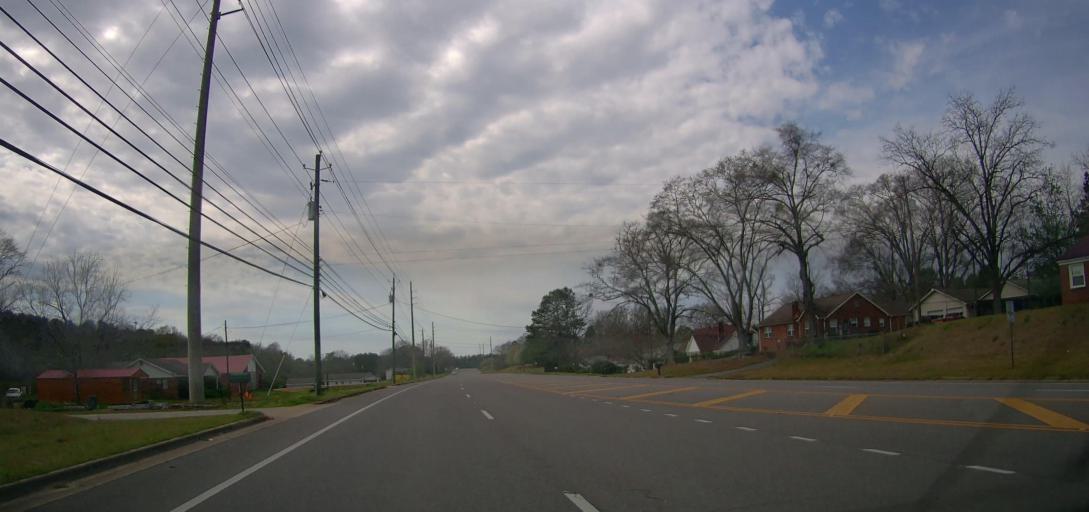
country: US
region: Alabama
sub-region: Marion County
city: Winfield
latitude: 33.9296
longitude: -87.7740
